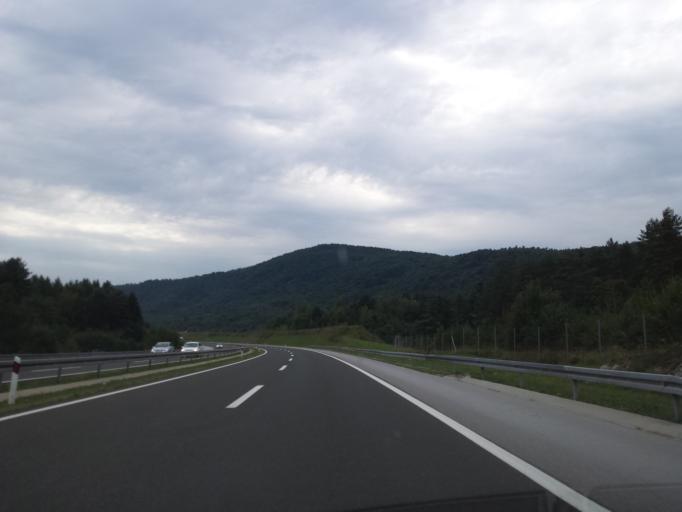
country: HR
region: Karlovacka
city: Ostarije
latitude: 45.1985
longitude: 15.2649
